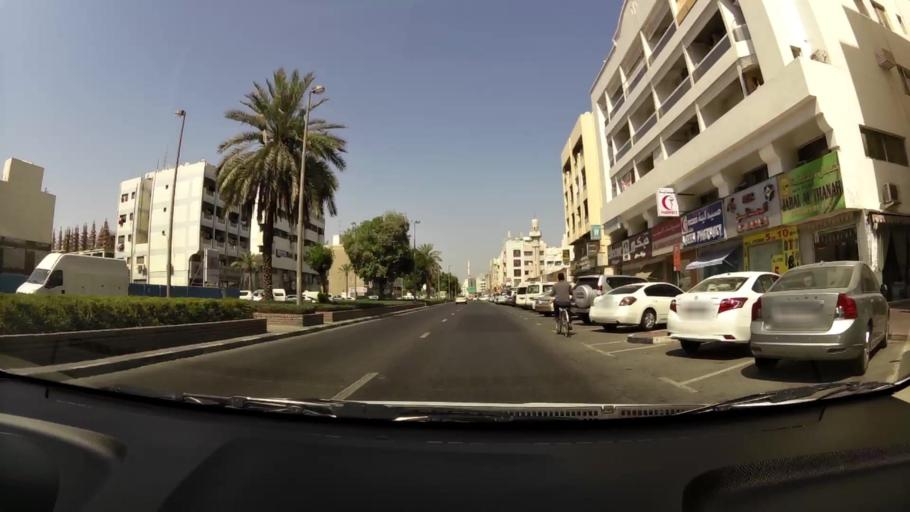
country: AE
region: Ash Shariqah
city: Sharjah
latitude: 25.2754
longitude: 55.3108
